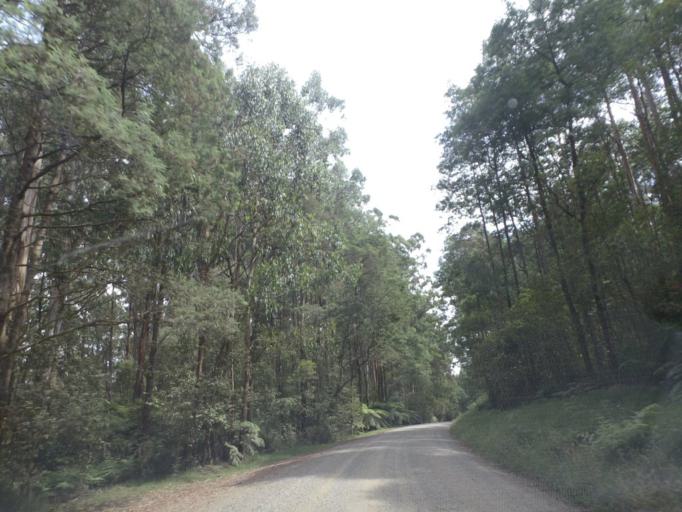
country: AU
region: Victoria
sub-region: Yarra Ranges
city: Healesville
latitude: -37.5475
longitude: 145.5144
